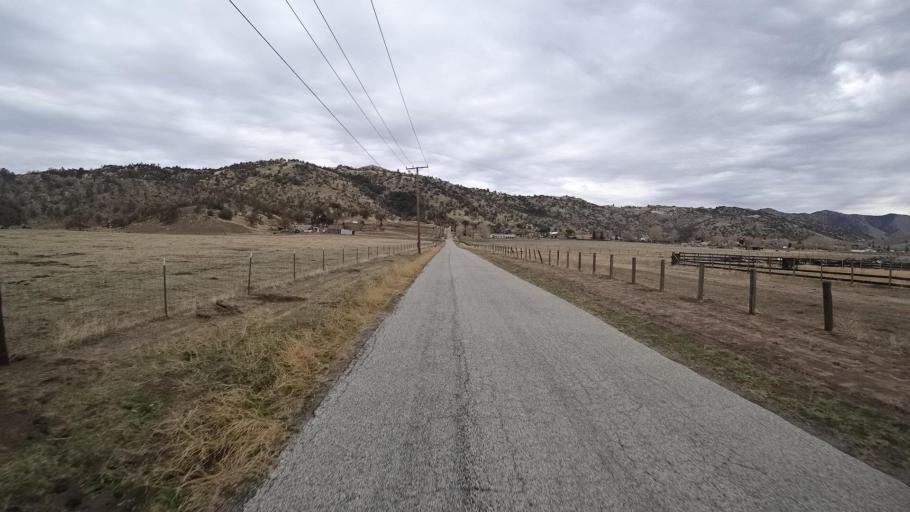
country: US
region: California
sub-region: Kern County
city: Stallion Springs
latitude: 35.1208
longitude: -118.6281
